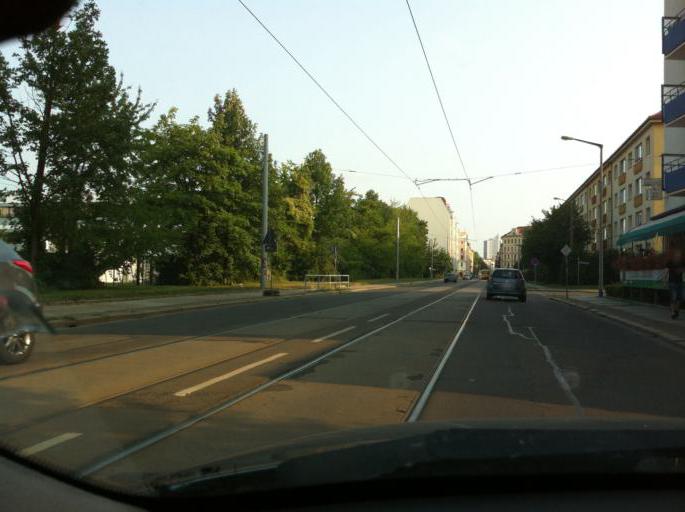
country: DE
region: Saxony
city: Leipzig
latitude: 51.3180
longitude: 12.3785
